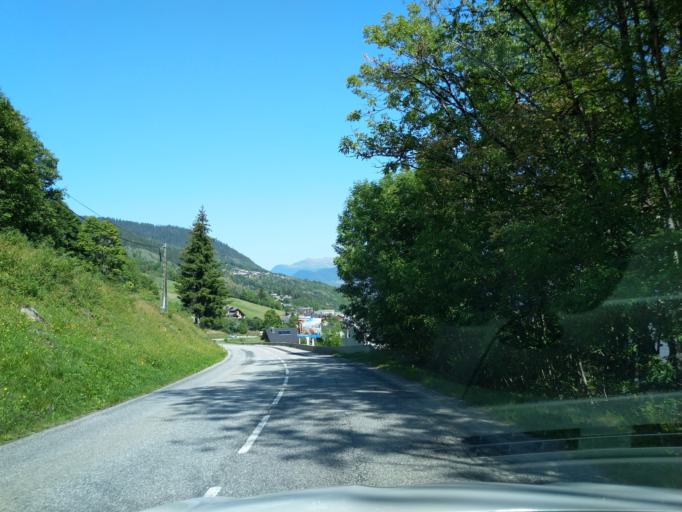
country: FR
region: Rhone-Alpes
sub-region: Departement de la Savoie
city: Les Allues
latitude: 45.4262
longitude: 6.5570
